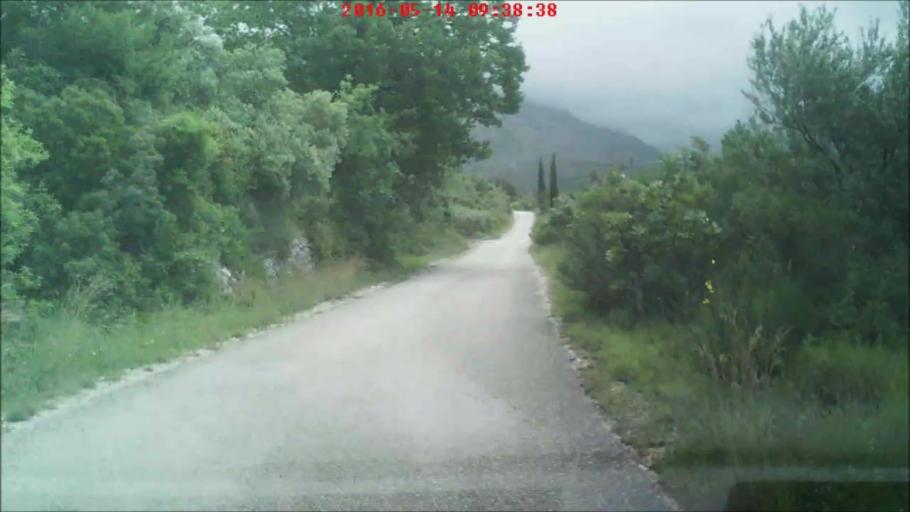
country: HR
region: Dubrovacko-Neretvanska
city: Podgora
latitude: 42.7915
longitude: 17.8881
